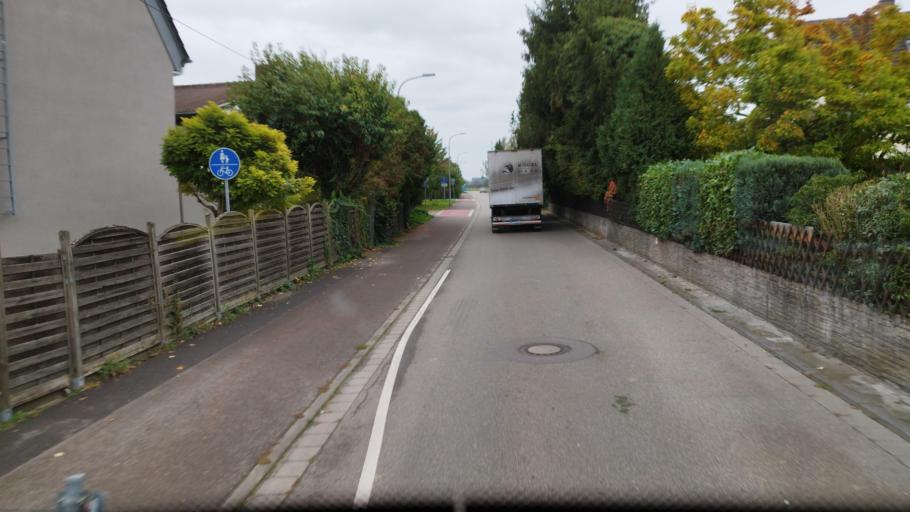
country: DE
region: Rheinland-Pfalz
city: Worth am Rhein
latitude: 49.0331
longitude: 8.2777
